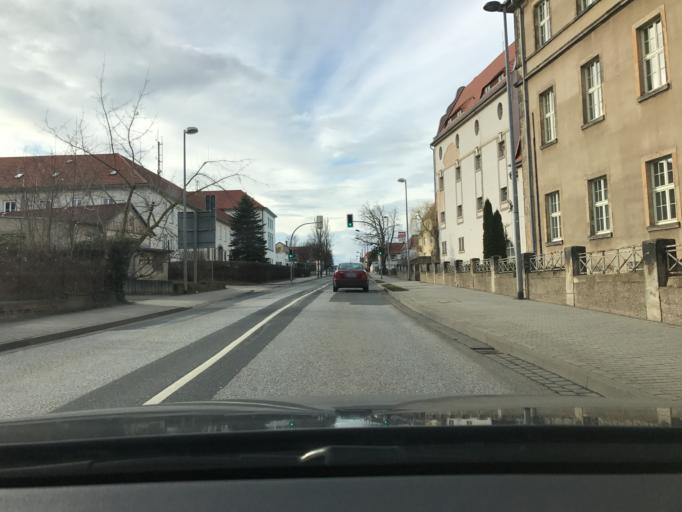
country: DE
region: Saxony-Anhalt
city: Wimmelburg
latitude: 51.5210
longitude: 11.5466
